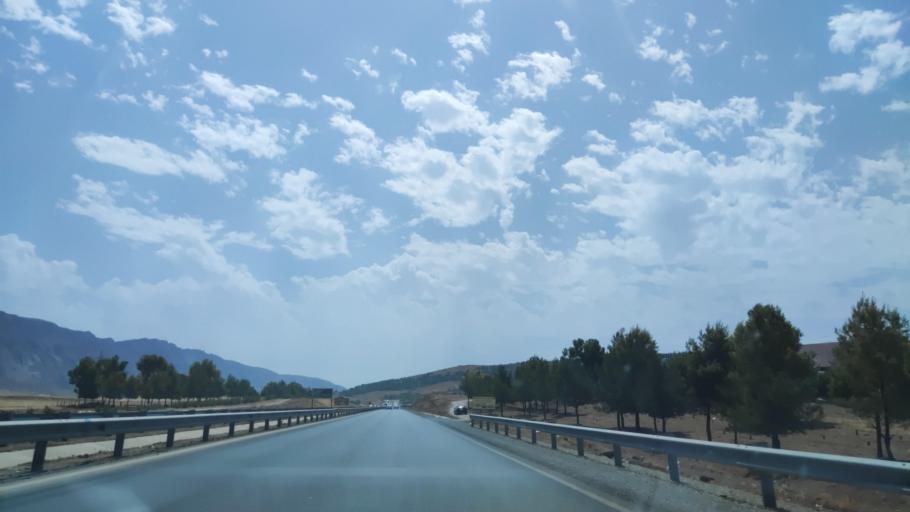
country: IQ
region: Arbil
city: Shaqlawah
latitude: 36.5027
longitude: 44.3553
